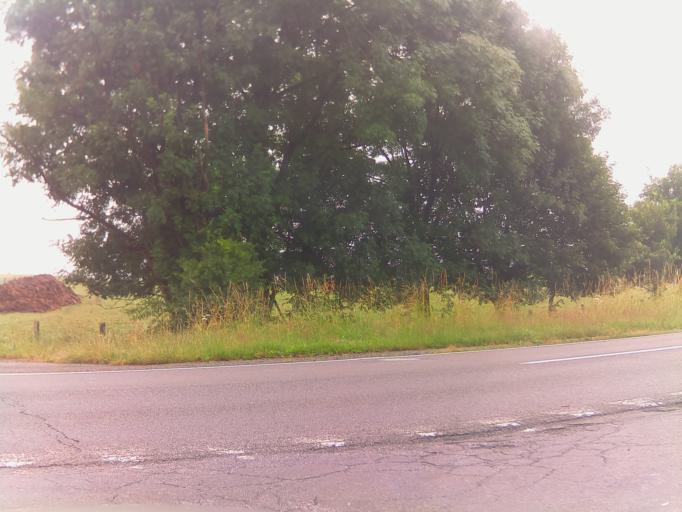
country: BE
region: Wallonia
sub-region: Province du Luxembourg
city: Neufchateau
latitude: 49.9036
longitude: 5.3733
